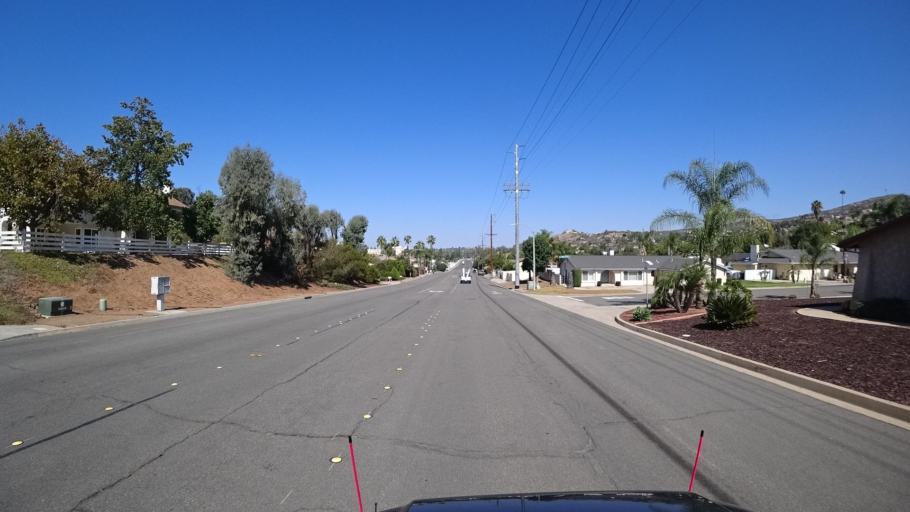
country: US
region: California
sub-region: San Diego County
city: Granite Hills
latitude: 32.7950
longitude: -116.9015
